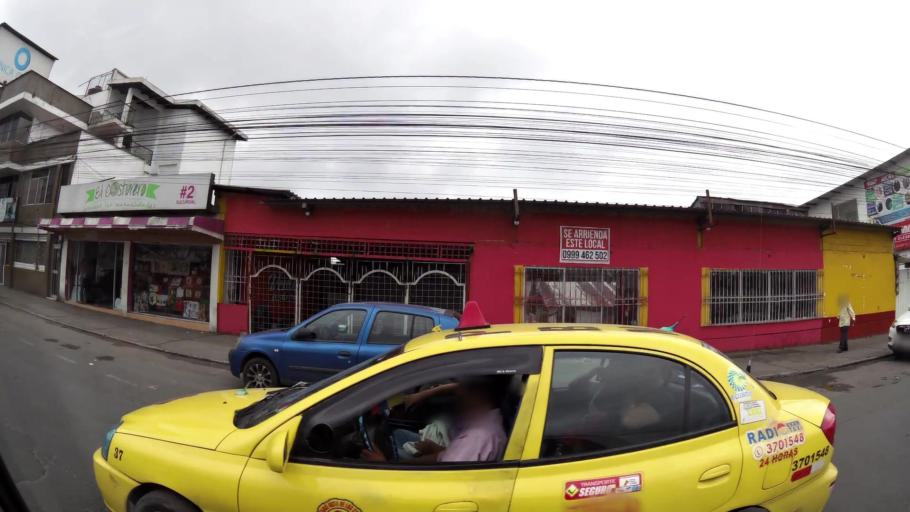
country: EC
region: Santo Domingo de los Tsachilas
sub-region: Canton Santo Domingo de los Colorados
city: Santo Domingo de los Colorados
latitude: -0.2488
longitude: -79.1587
